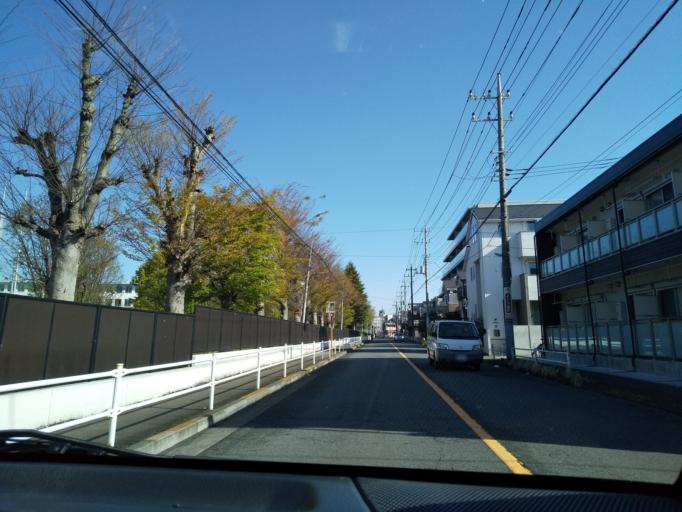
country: JP
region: Tokyo
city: Hino
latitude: 35.6907
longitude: 139.4339
